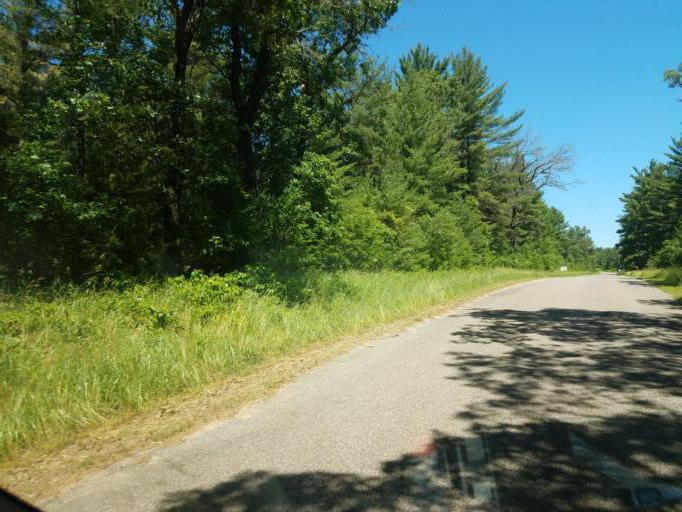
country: US
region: Wisconsin
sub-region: Adams County
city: Friendship
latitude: 44.0160
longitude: -89.9556
